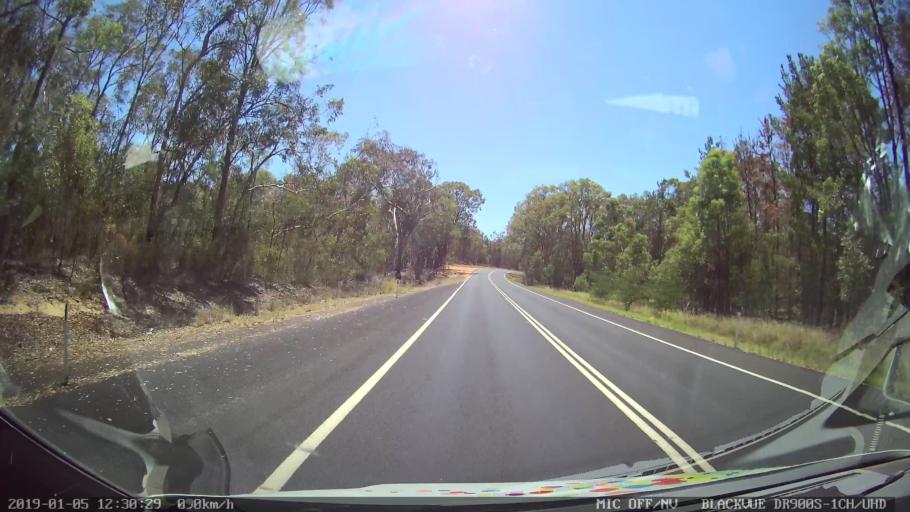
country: AU
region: New South Wales
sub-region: Warrumbungle Shire
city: Coonabarabran
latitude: -31.2273
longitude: 149.3510
